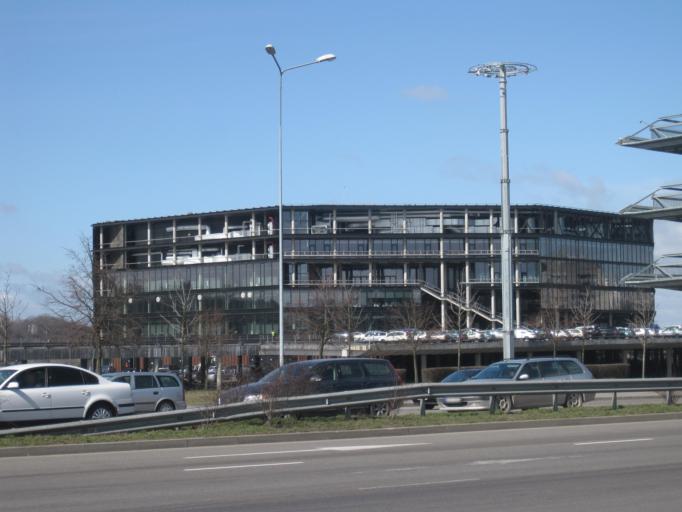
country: LT
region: Kauno apskritis
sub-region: Kaunas
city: Aleksotas
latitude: 54.8903
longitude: 23.9177
